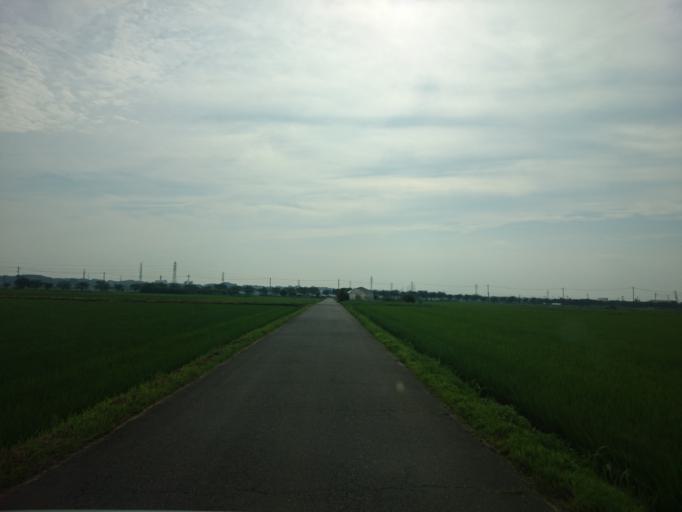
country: JP
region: Ibaraki
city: Tsukuba
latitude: 36.1687
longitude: 140.1017
